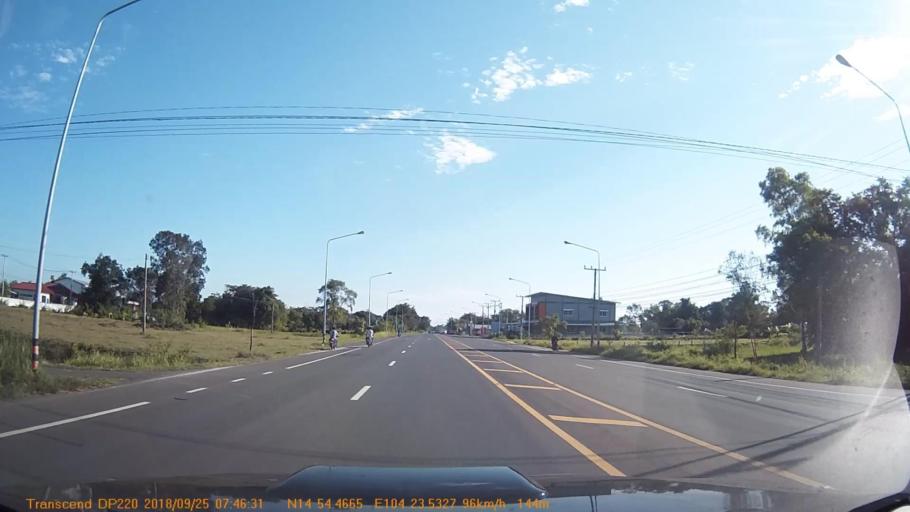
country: TH
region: Sisaket
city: Phayu
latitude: 14.9080
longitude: 104.3923
